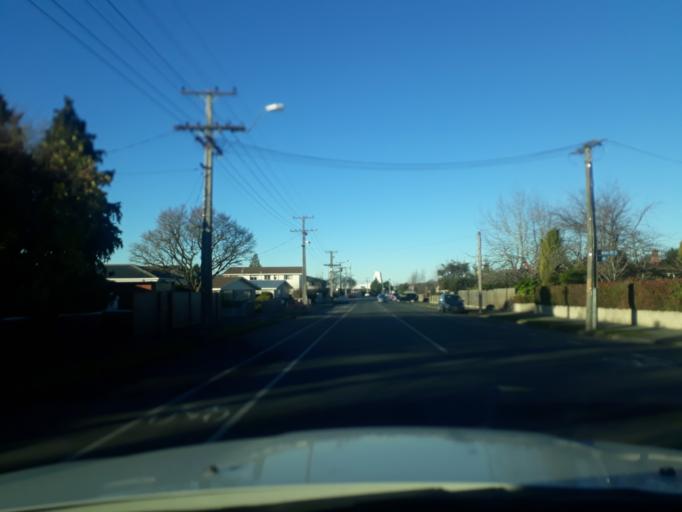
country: NZ
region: Canterbury
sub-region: Timaru District
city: Timaru
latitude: -44.3875
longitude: 171.1984
